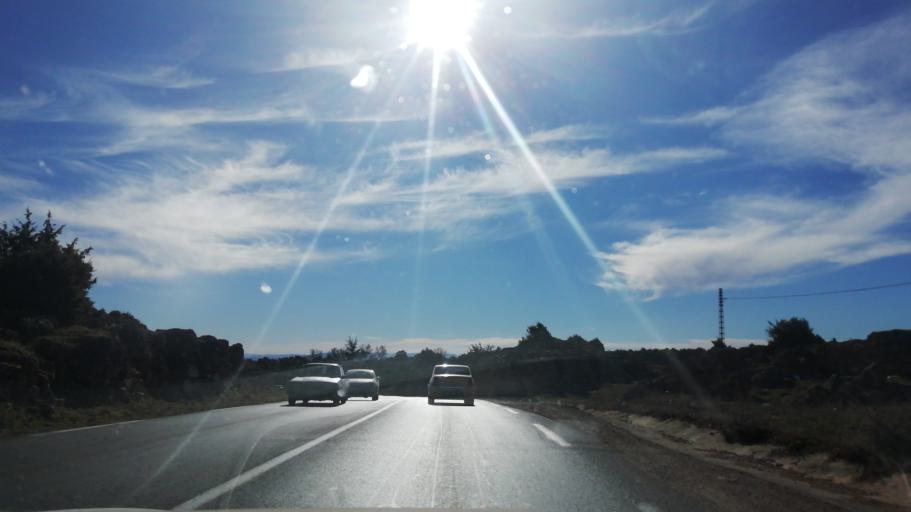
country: DZ
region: Tlemcen
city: Mansoura
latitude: 34.7528
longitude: -1.3442
